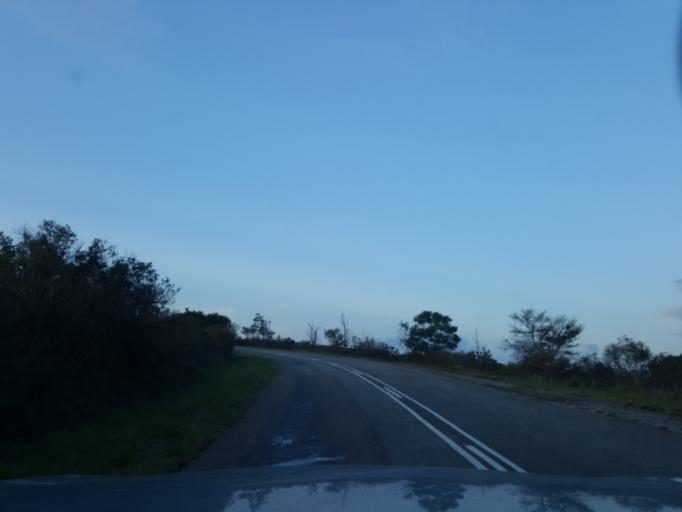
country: ZA
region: Eastern Cape
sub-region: Cacadu District Municipality
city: Grahamstown
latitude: -33.4617
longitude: 26.4959
